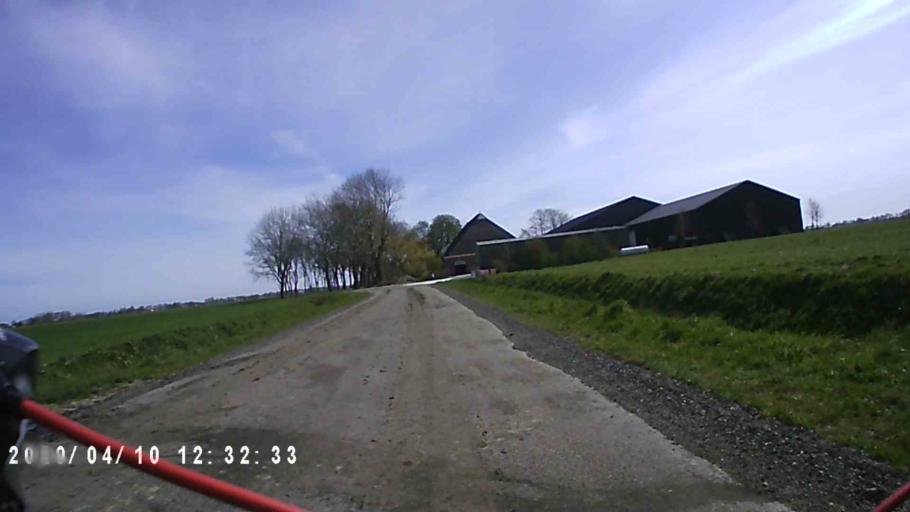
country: NL
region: Groningen
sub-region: Gemeente De Marne
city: Ulrum
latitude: 53.3954
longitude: 6.4114
